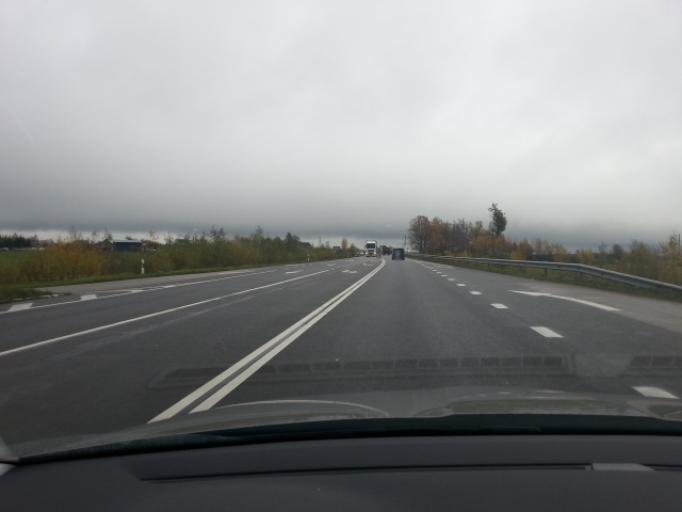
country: LT
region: Kauno apskritis
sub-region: Kauno rajonas
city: Mastaiciai
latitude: 54.7615
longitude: 23.7499
